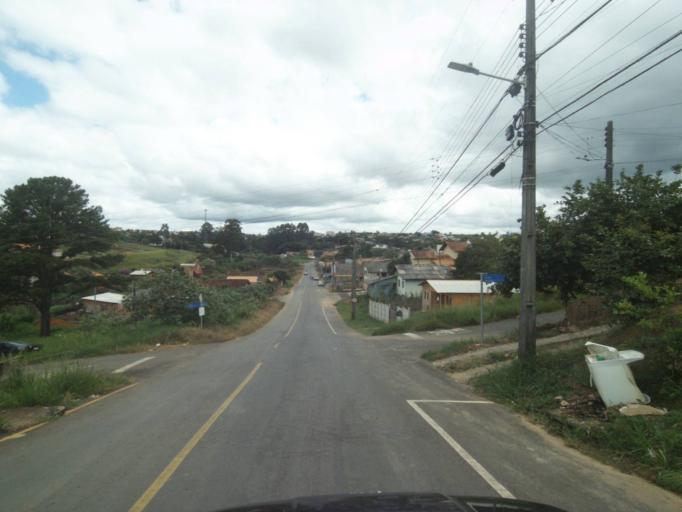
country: BR
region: Parana
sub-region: Telemaco Borba
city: Telemaco Borba
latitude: -24.3136
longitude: -50.6448
